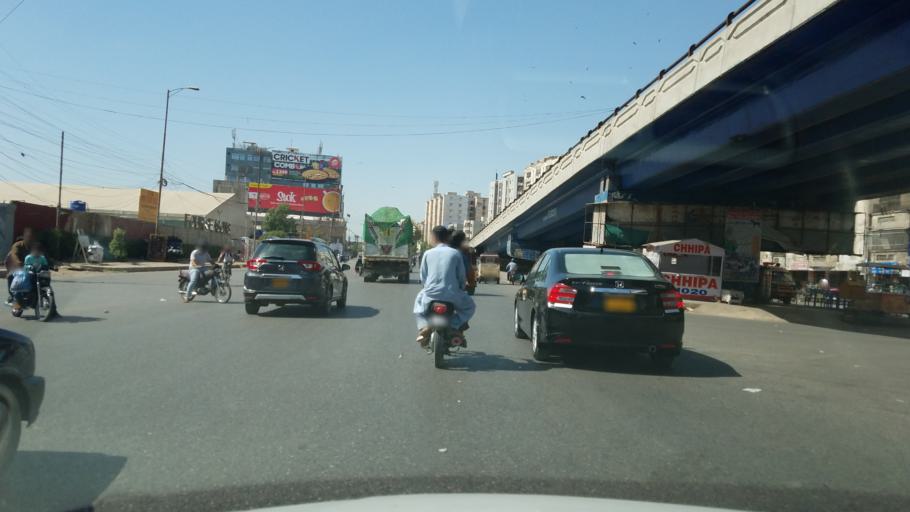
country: PK
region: Sindh
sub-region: Karachi District
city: Karachi
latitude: 24.9047
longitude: 67.1131
